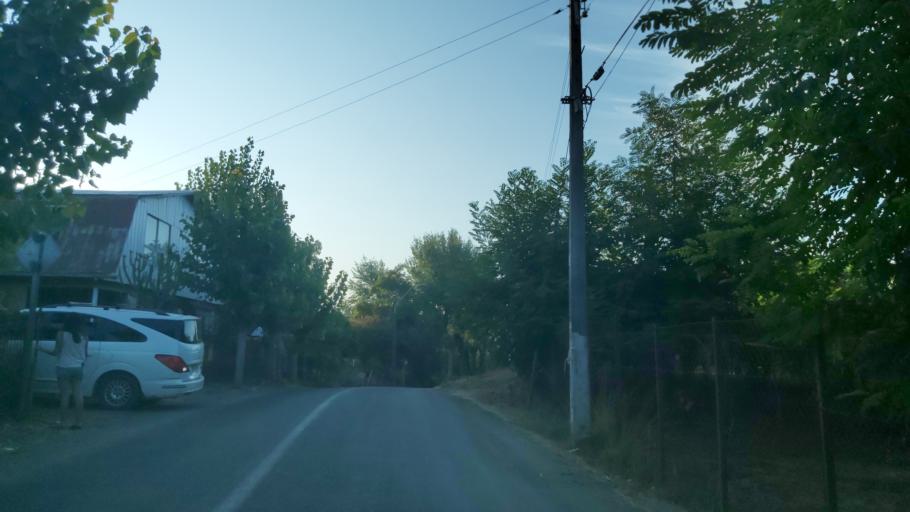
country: CL
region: Biobio
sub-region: Provincia de Biobio
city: La Laja
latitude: -37.1627
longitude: -72.9136
